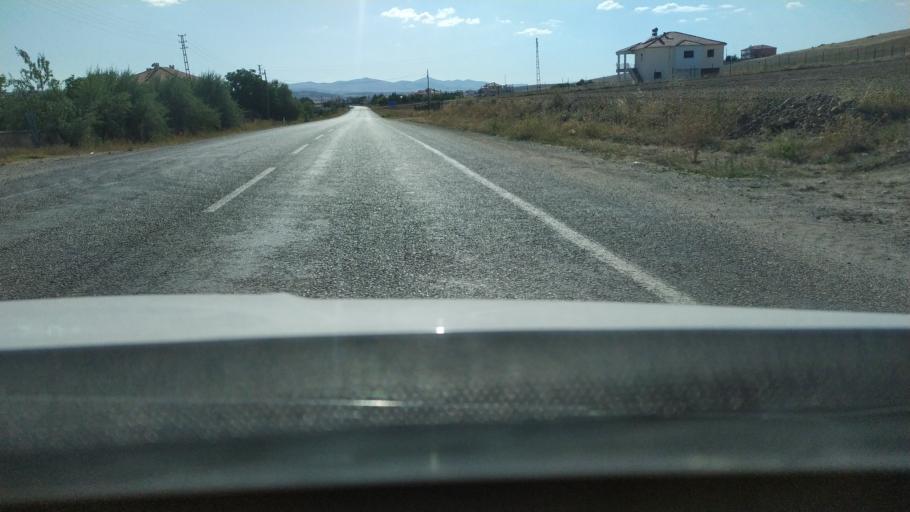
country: TR
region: Kayseri
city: Felahiye
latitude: 39.1043
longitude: 35.5945
